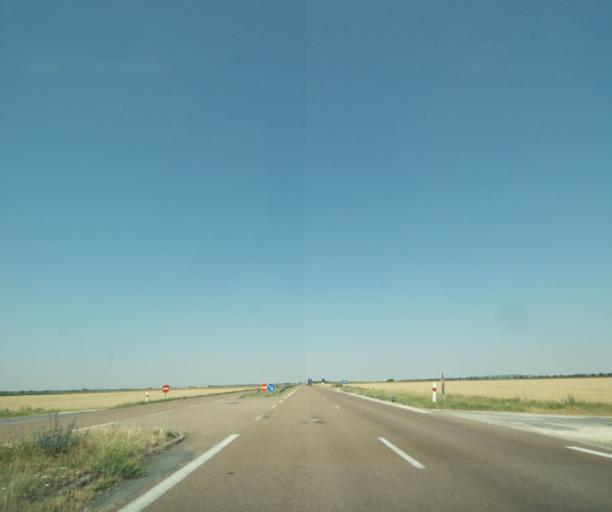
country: FR
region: Champagne-Ardenne
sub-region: Departement de la Marne
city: Frignicourt
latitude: 48.6962
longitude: 4.6940
